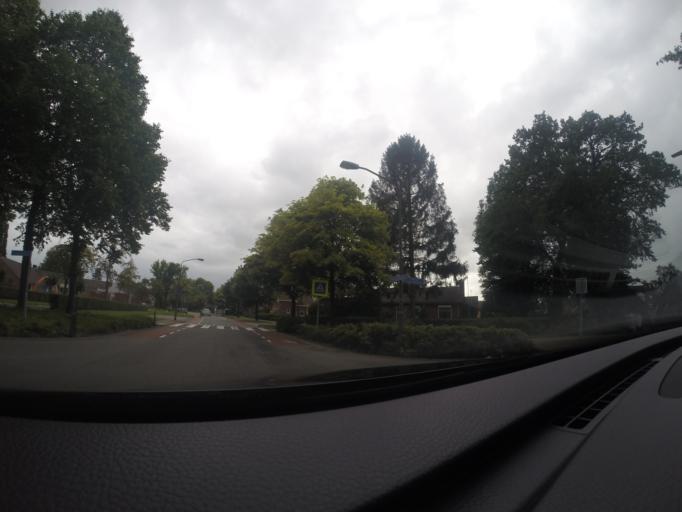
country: NL
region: Overijssel
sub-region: Gemeente Hof van Twente
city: Markelo
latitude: 52.2370
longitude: 6.4973
